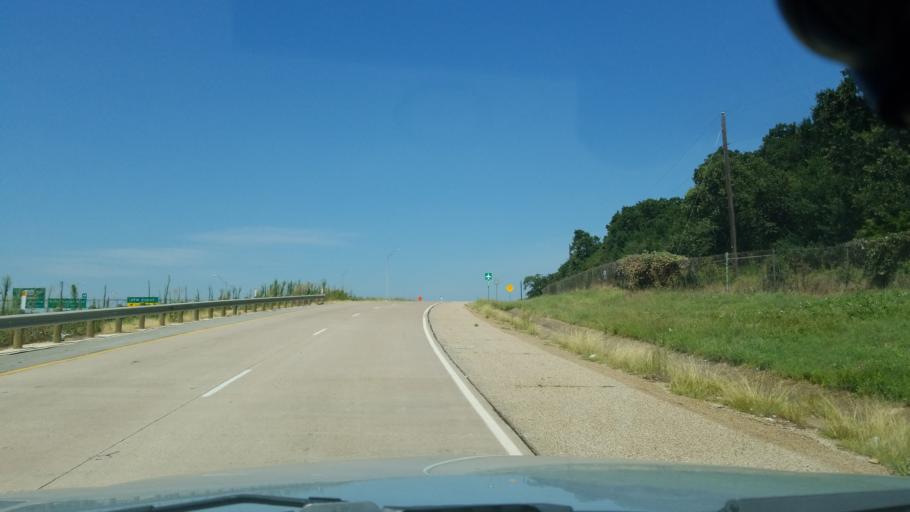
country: US
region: Texas
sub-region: Tarrant County
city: Euless
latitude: 32.8375
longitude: -97.0307
